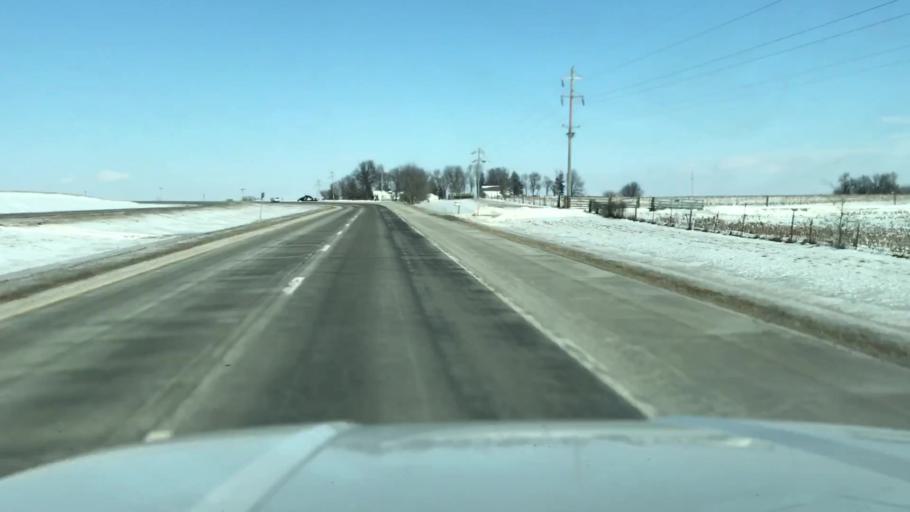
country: US
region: Missouri
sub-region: Nodaway County
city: Maryville
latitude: 40.2687
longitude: -94.8665
